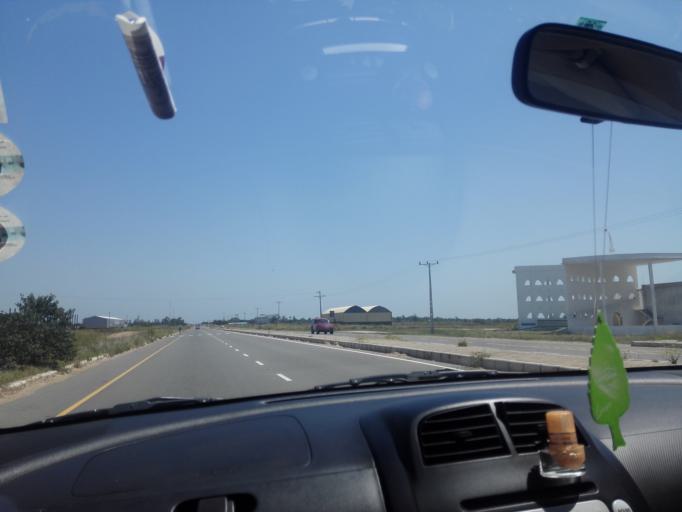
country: MZ
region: Maputo City
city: Maputo
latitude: -25.8247
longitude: 32.6721
